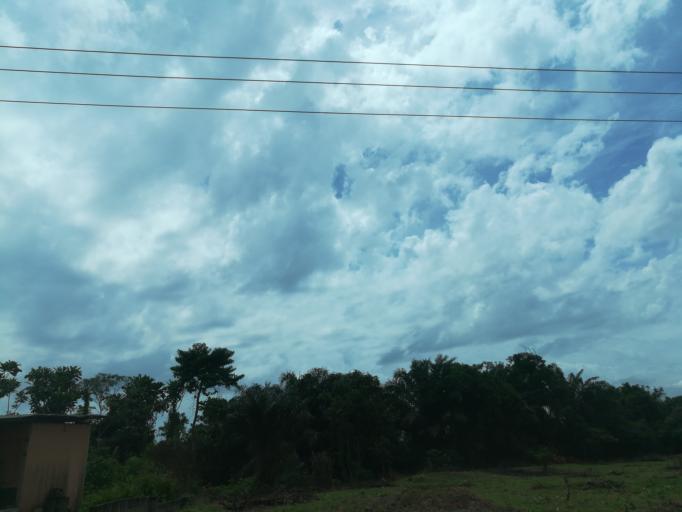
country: NG
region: Lagos
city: Ejirin
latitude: 6.6269
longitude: 3.7068
